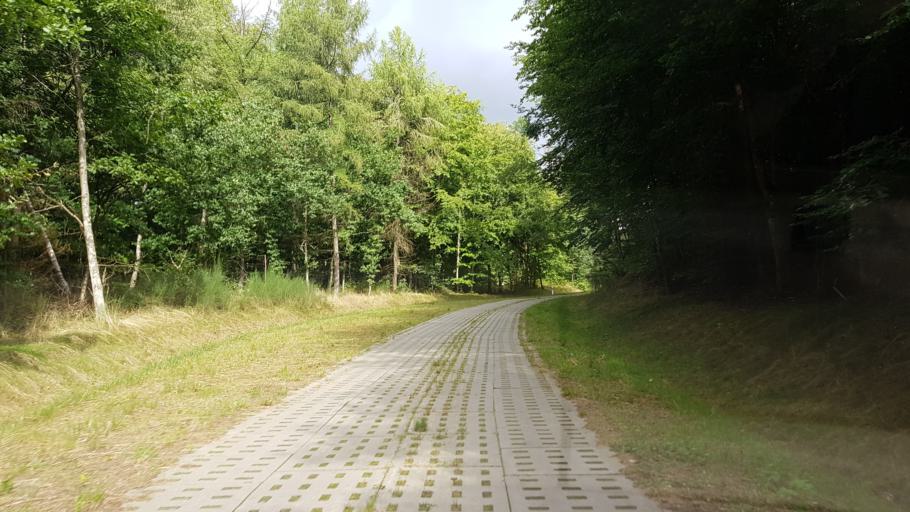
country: PL
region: West Pomeranian Voivodeship
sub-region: Powiat bialogardzki
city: Tychowo
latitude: 53.9788
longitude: 16.3870
